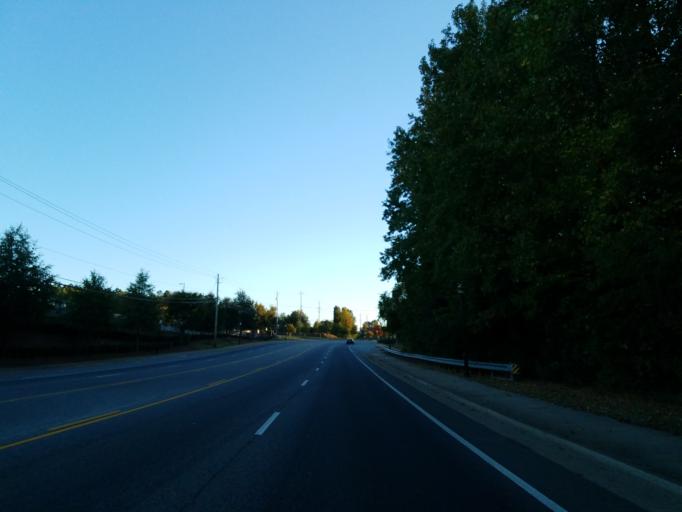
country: US
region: Georgia
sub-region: Forsyth County
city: Cumming
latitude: 34.1918
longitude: -84.1404
